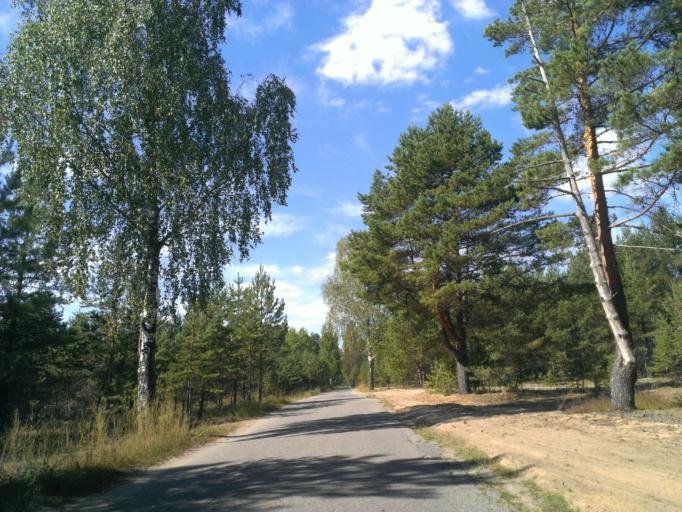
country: LV
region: Adazi
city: Adazi
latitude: 57.1047
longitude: 24.3774
